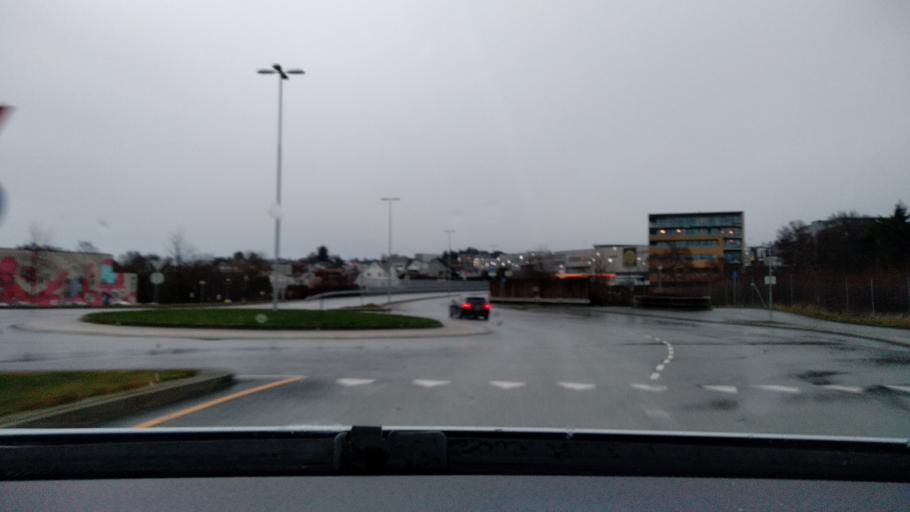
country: NO
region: Rogaland
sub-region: Stavanger
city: Stavanger
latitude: 58.9530
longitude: 5.6708
